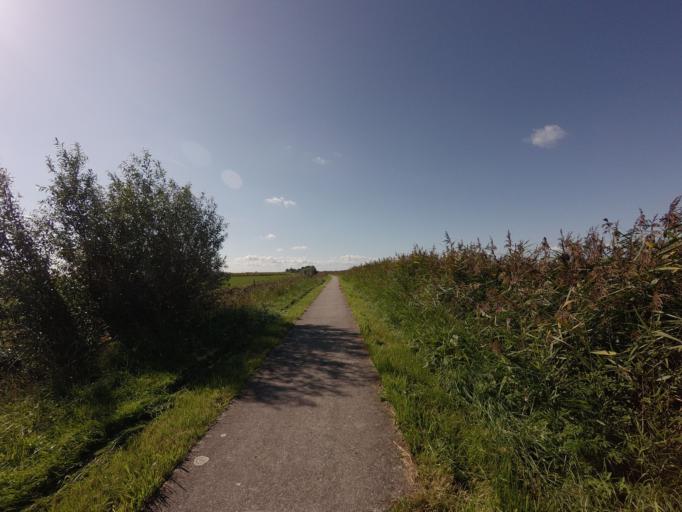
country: NL
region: Friesland
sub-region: Gemeente Boarnsterhim
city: Reduzum
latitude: 53.1345
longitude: 5.7583
